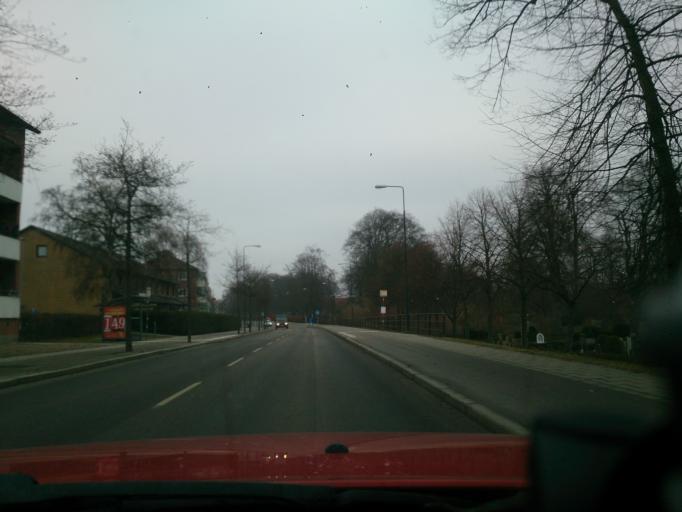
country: SE
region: Skane
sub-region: Ystads Kommun
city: Ystad
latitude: 55.4292
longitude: 13.8110
